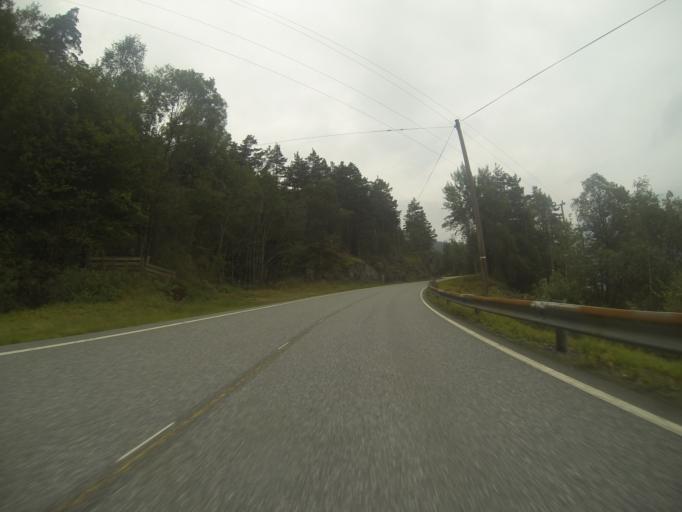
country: NO
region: Rogaland
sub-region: Suldal
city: Sand
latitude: 59.5251
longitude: 6.2460
